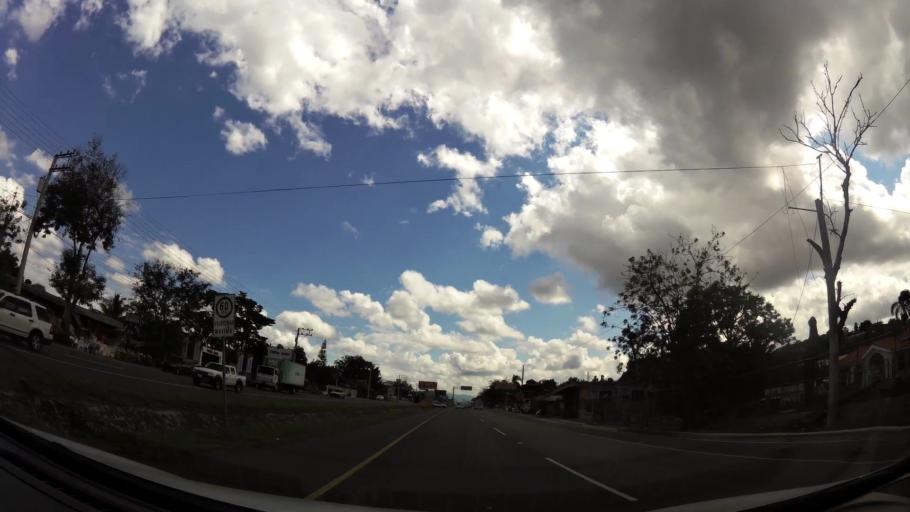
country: DO
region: La Vega
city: Rio Verde Arriba
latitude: 19.3535
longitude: -70.6008
